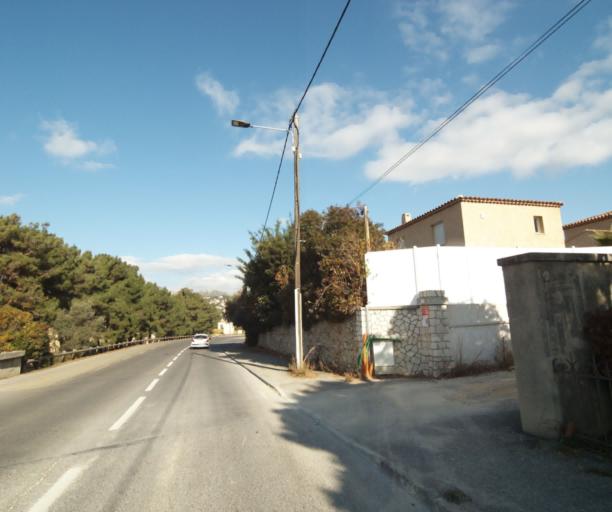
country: FR
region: Provence-Alpes-Cote d'Azur
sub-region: Departement des Bouches-du-Rhone
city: Allauch
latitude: 43.3514
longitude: 5.4878
